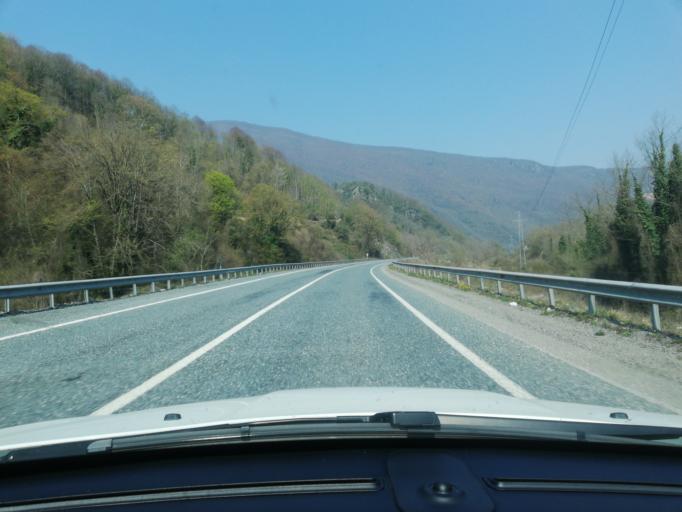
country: TR
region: Zonguldak
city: Gokcebey
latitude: 41.2569
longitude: 32.1587
